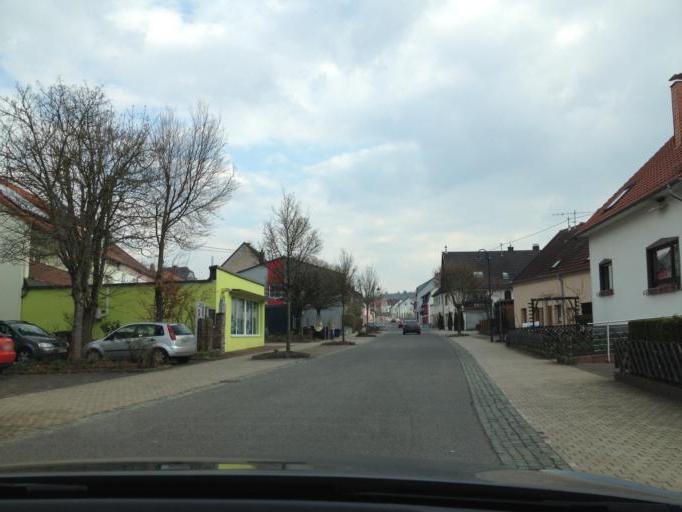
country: DE
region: Saarland
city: Freisen
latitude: 49.5521
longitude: 7.2489
